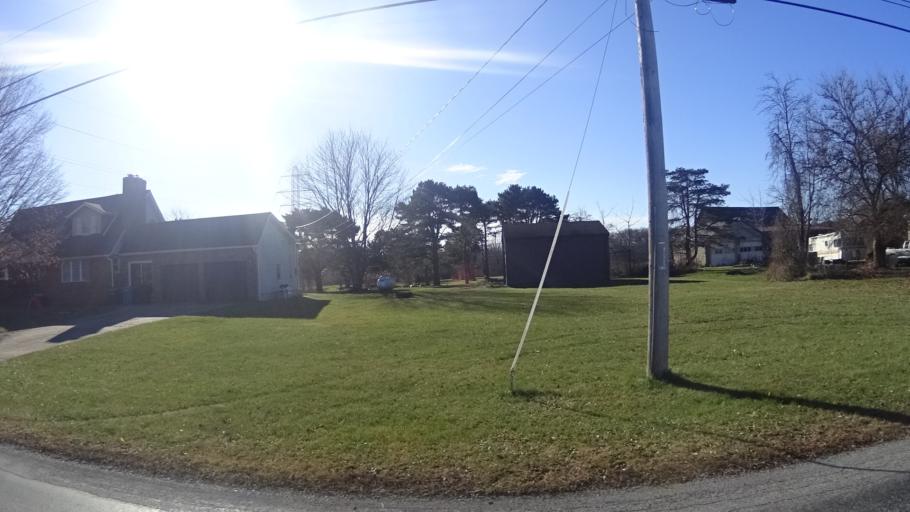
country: US
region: Ohio
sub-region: Lorain County
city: South Amherst
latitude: 41.3761
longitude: -82.2658
